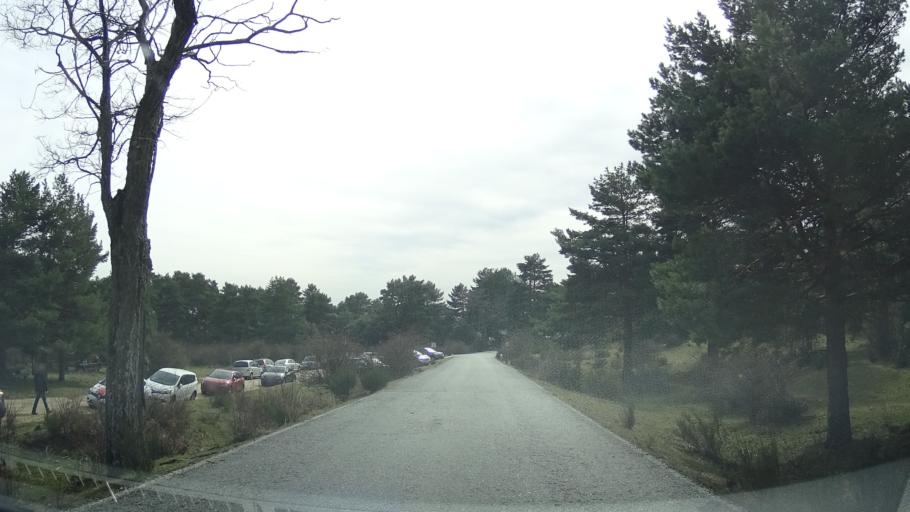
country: ES
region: Madrid
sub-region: Provincia de Madrid
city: Navacerrada
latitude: 40.7492
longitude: -3.9939
